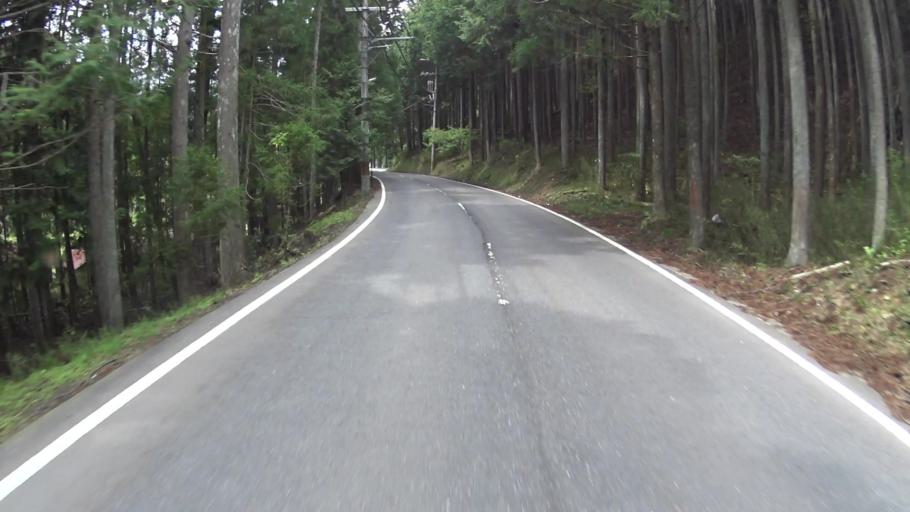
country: JP
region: Kyoto
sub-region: Kyoto-shi
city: Kamigyo-ku
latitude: 35.1939
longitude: 135.7045
